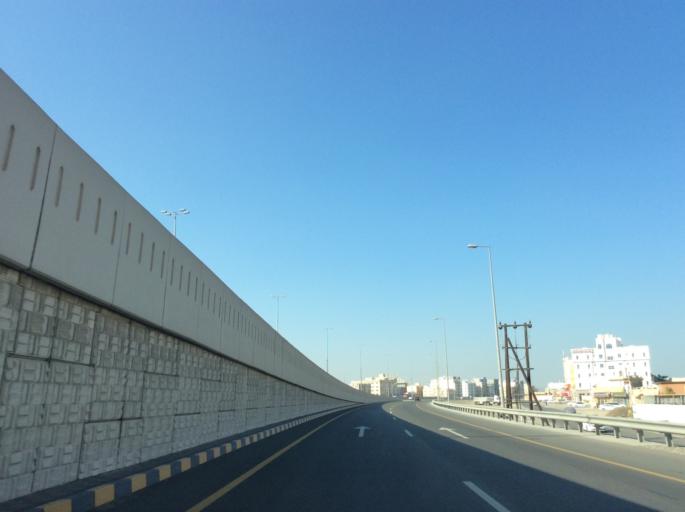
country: OM
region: Al Batinah
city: Al Liwa'
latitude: 24.4267
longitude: 56.6094
